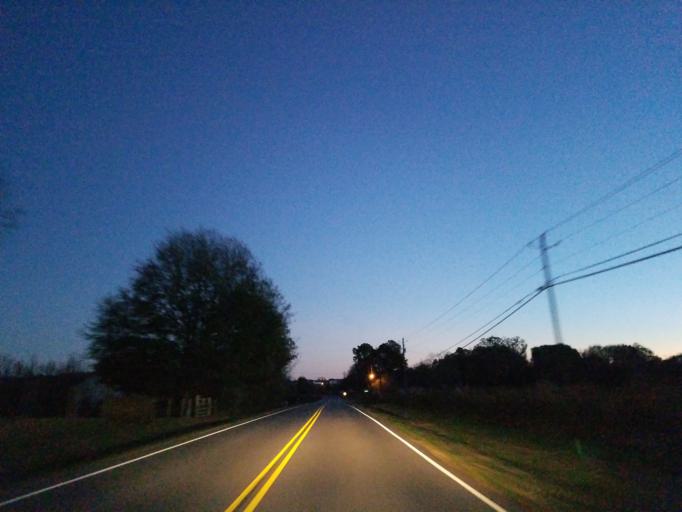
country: US
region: Georgia
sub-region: Forsyth County
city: Cumming
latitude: 34.3114
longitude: -84.1060
